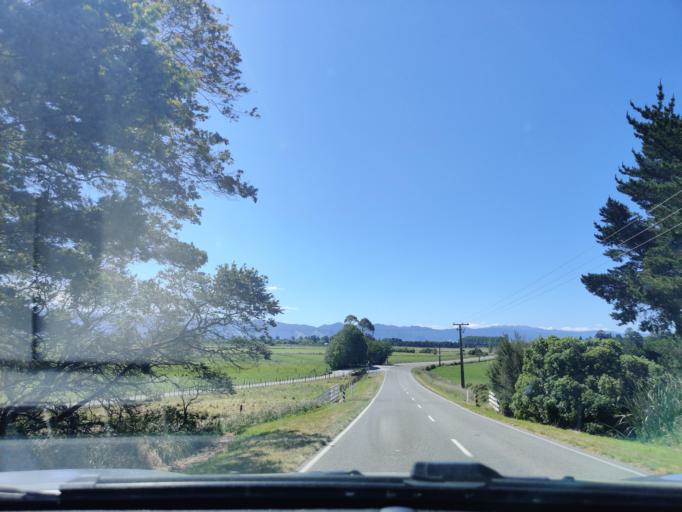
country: NZ
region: Wellington
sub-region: South Wairarapa District
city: Waipawa
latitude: -41.3012
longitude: 175.2707
